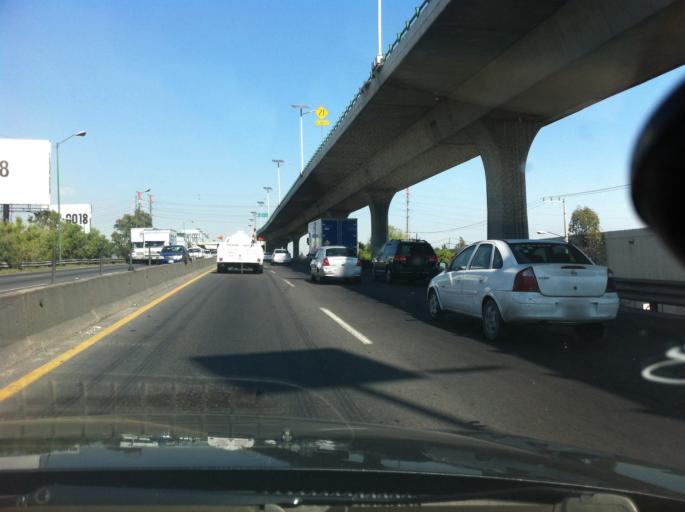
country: MX
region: Mexico
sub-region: Tultitlan
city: Buenavista
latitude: 19.6142
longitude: -99.1907
